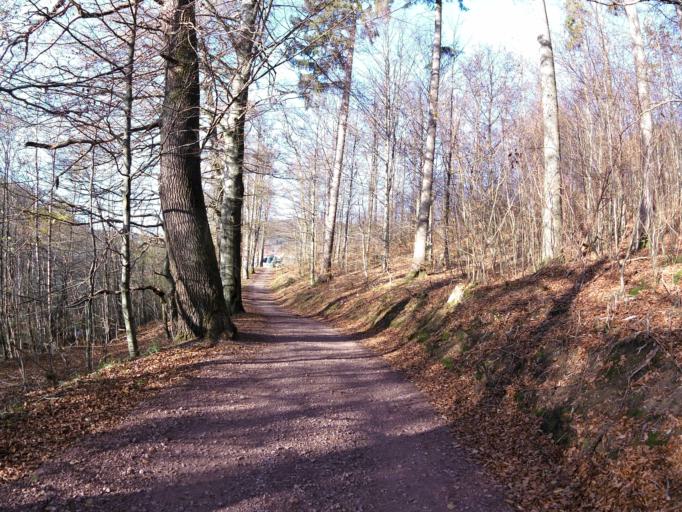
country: DE
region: Thuringia
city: Ruhla
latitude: 50.8784
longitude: 10.3889
